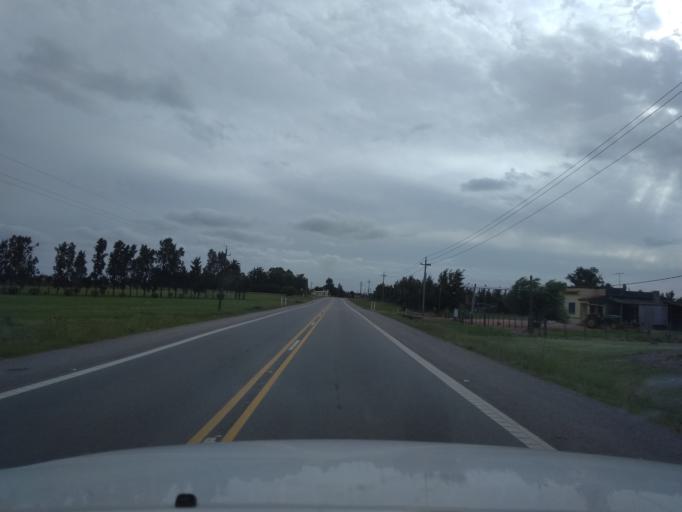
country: UY
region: Canelones
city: Joaquin Suarez
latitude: -34.7008
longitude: -56.0401
